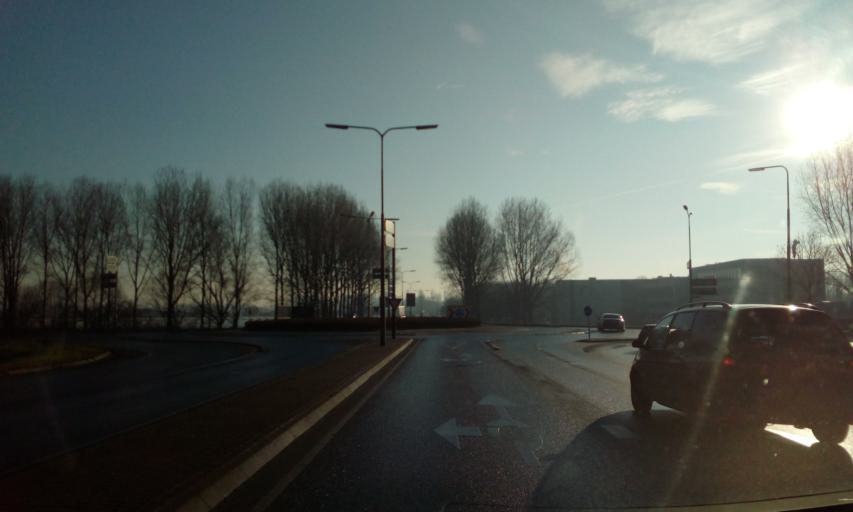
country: NL
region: South Holland
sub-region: Gemeente Krimpen aan den IJssel
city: Krimpen aan den IJssel
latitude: 51.9795
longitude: 4.6191
